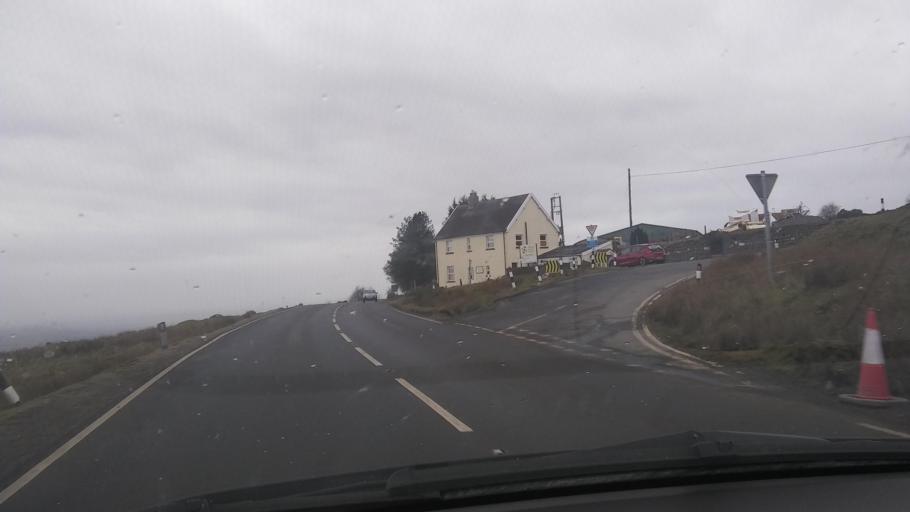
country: GB
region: England
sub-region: Worcestershire
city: Tenbury Wells
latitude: 52.3759
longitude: -2.5929
